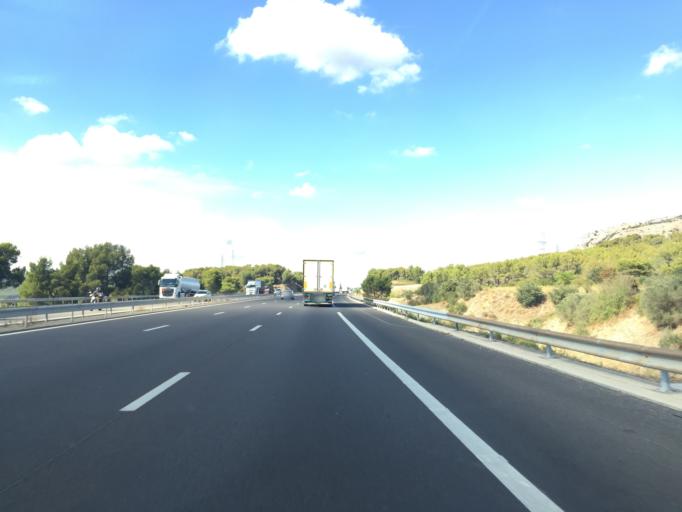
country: FR
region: Provence-Alpes-Cote d'Azur
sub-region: Departement des Bouches-du-Rhone
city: Salon-de-Provence
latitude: 43.6681
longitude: 5.0970
